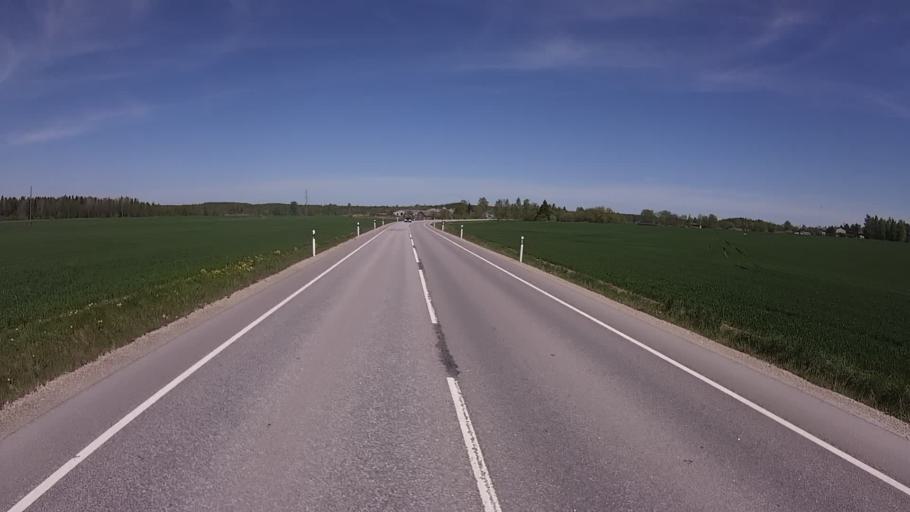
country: EE
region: Vorumaa
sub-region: Voru linn
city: Voru
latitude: 57.8662
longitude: 27.1045
